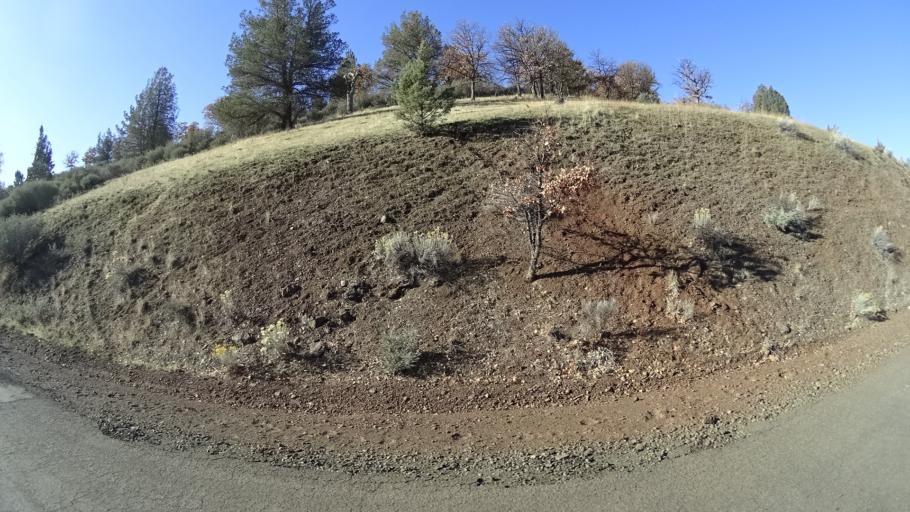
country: US
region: California
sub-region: Siskiyou County
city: Montague
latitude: 41.9146
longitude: -122.4425
